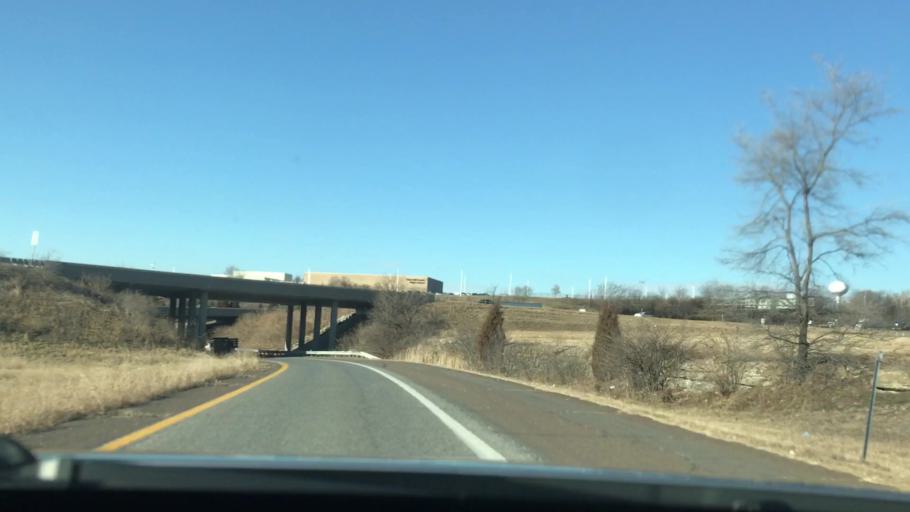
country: US
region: Missouri
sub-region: Platte County
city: Riverside
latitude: 39.1725
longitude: -94.6219
